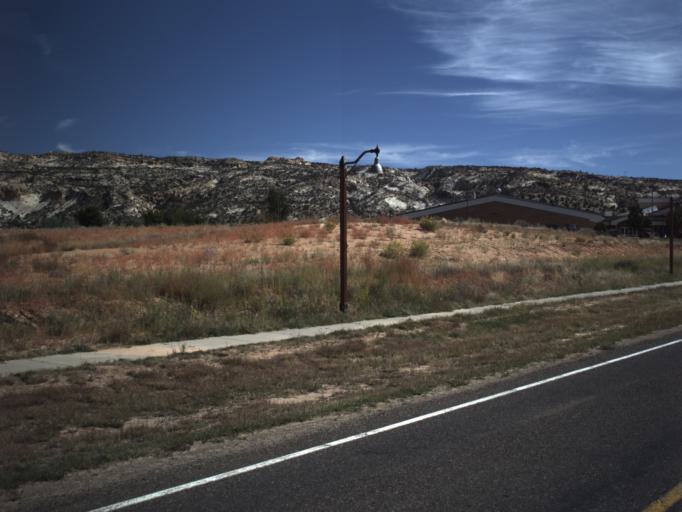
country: US
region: Utah
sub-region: Wayne County
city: Loa
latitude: 37.7660
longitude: -111.5894
